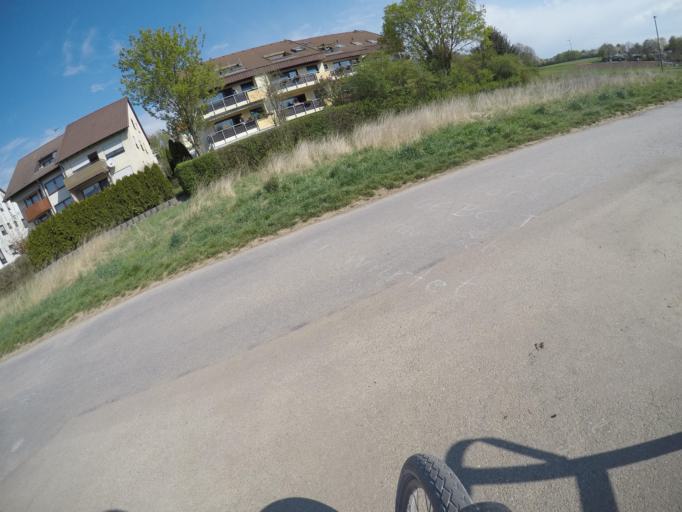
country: DE
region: Baden-Wuerttemberg
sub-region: Regierungsbezirk Stuttgart
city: Ditzingen
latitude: 48.8268
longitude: 9.0772
